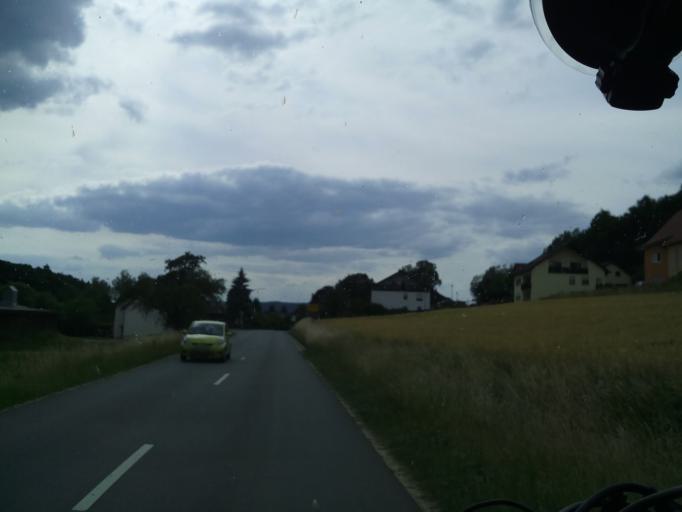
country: DE
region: Bavaria
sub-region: Regierungsbezirk Unterfranken
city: Untermerzbach
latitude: 50.1023
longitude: 10.9045
